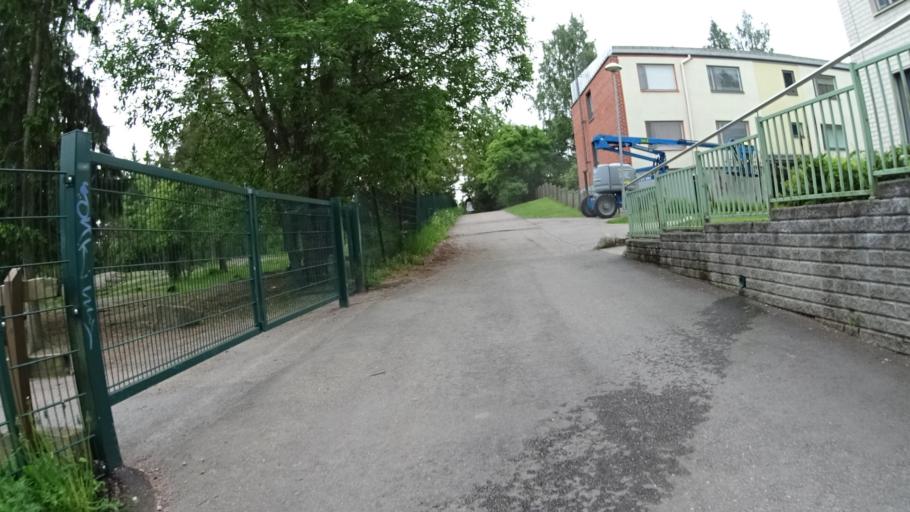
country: FI
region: Uusimaa
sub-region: Helsinki
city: Kilo
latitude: 60.2798
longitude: 24.8449
